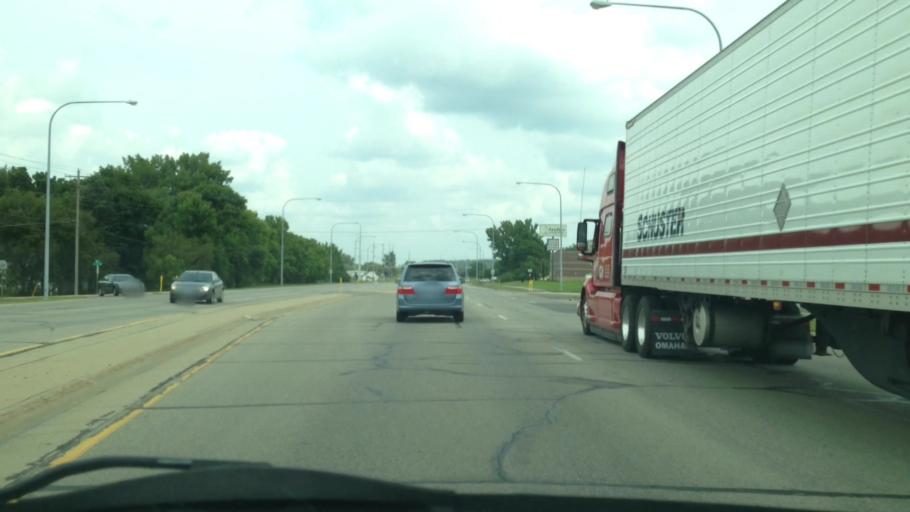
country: US
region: Minnesota
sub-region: Olmsted County
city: Rochester
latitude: 44.0551
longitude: -92.4545
